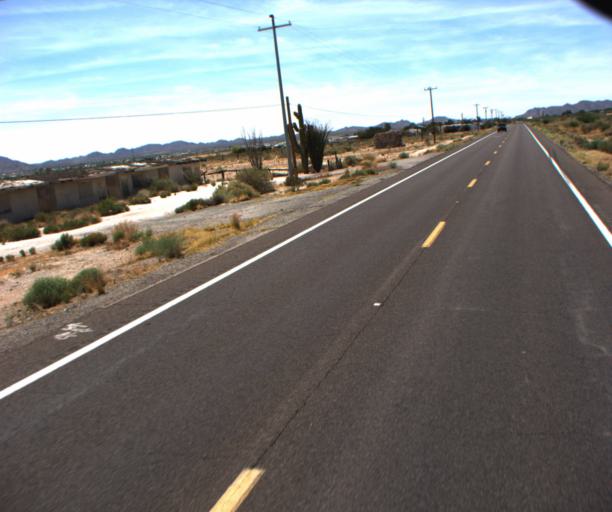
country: US
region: Arizona
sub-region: La Paz County
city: Salome
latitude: 33.7895
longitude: -113.6008
